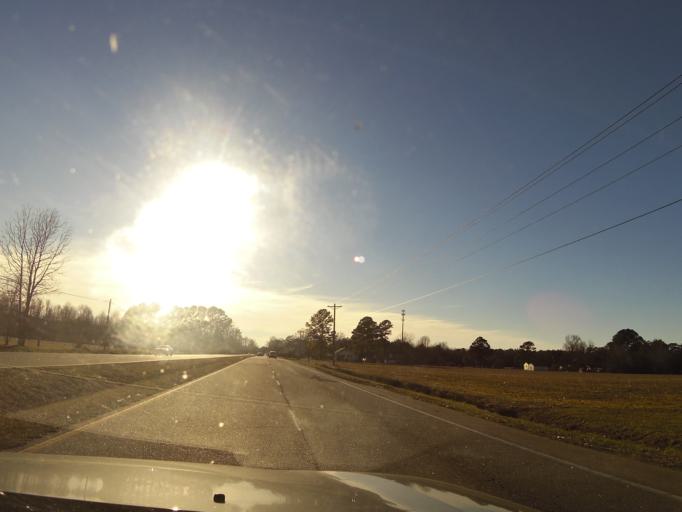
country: US
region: Virginia
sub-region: Isle of Wight County
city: Windsor
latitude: 36.6992
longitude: -76.7073
